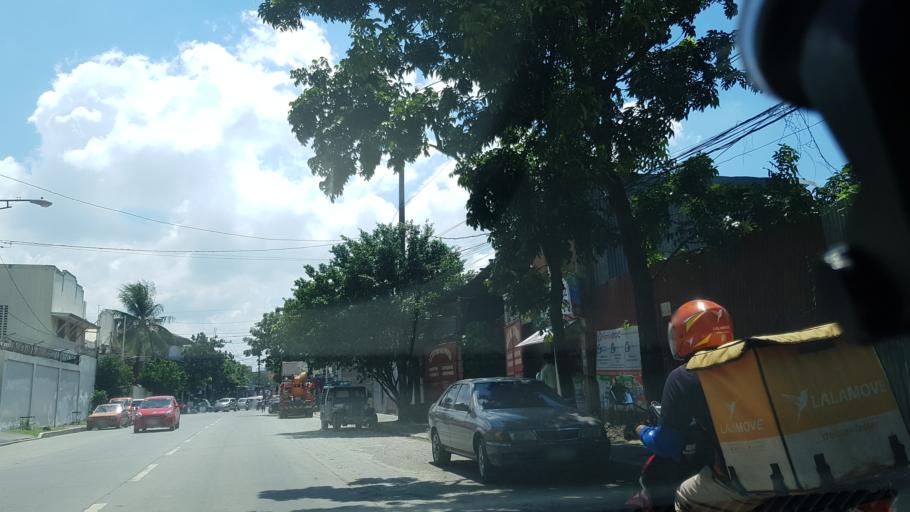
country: PH
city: Sambayanihan People's Village
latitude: 14.4641
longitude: 120.9961
